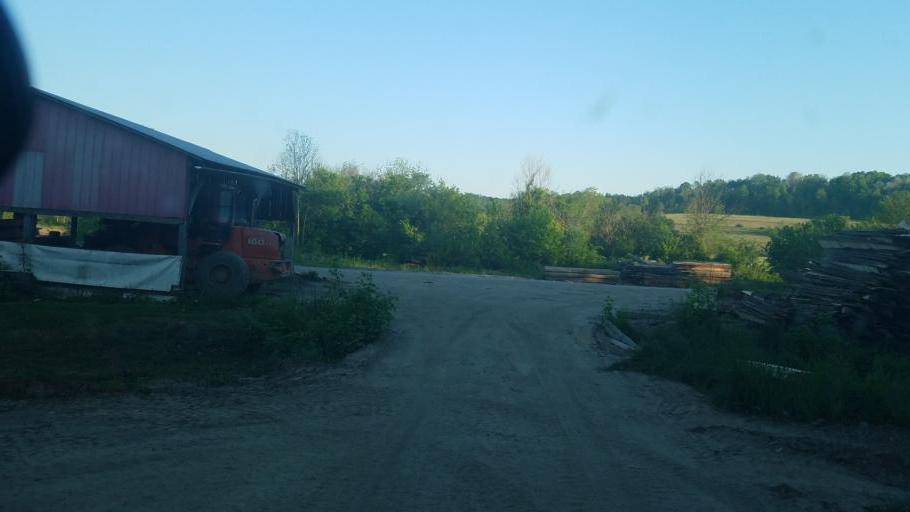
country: US
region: Ohio
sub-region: Belmont County
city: Barnesville
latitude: 40.0255
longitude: -81.3296
